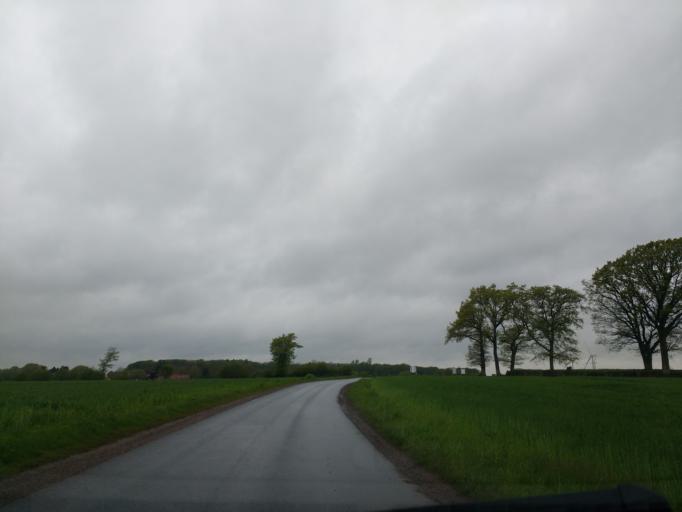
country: DE
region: Schleswig-Holstein
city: Loose
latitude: 54.5048
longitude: 9.9247
